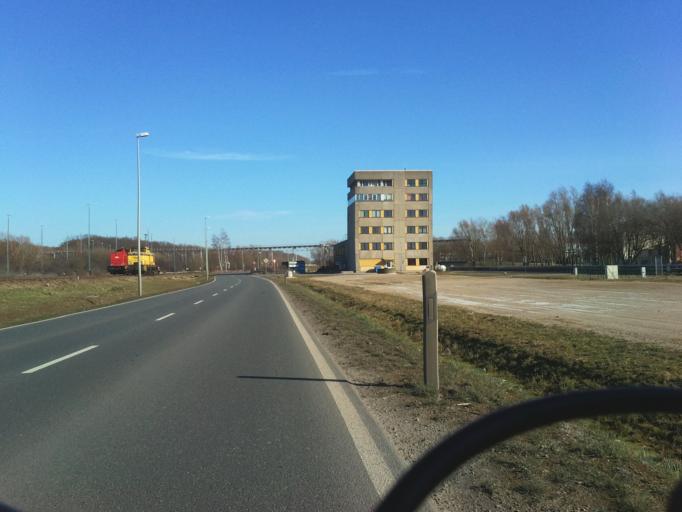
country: DE
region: Mecklenburg-Vorpommern
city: Nienhagen
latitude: 54.1463
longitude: 12.1440
